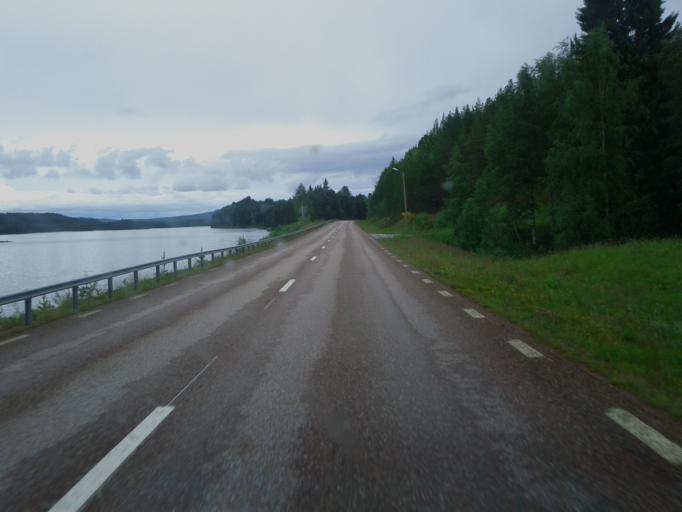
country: NO
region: Hedmark
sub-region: Trysil
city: Innbygda
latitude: 61.7425
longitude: 12.9759
